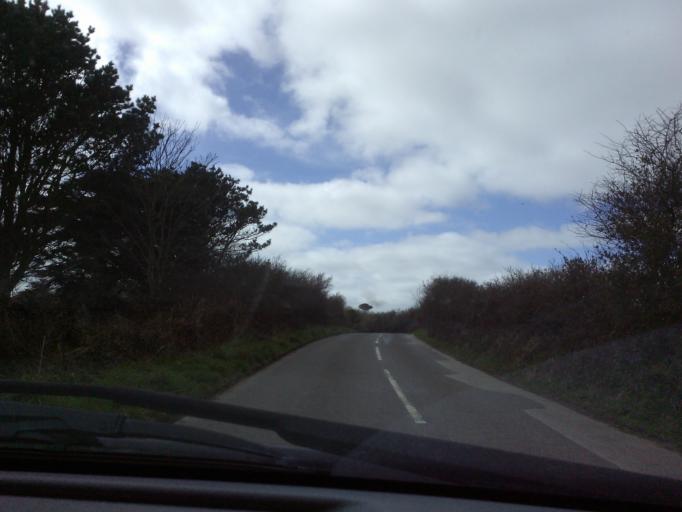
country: GB
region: England
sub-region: Cornwall
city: St. Buryan
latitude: 50.0605
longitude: -5.6296
